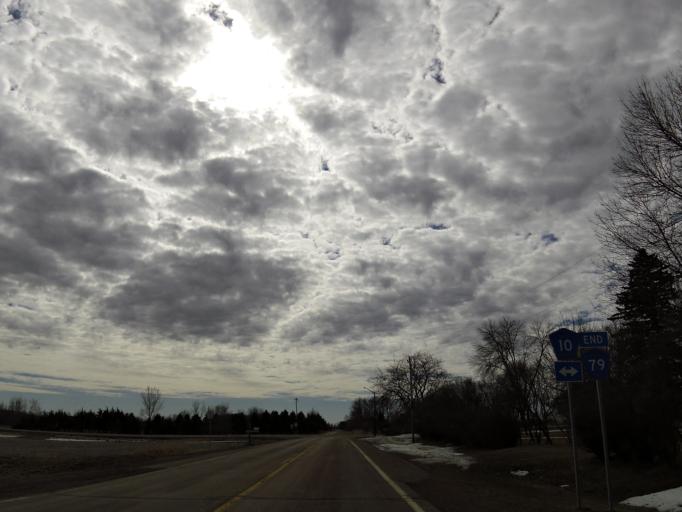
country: US
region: Minnesota
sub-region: Scott County
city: Prior Lake
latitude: 44.6536
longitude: -93.5164
